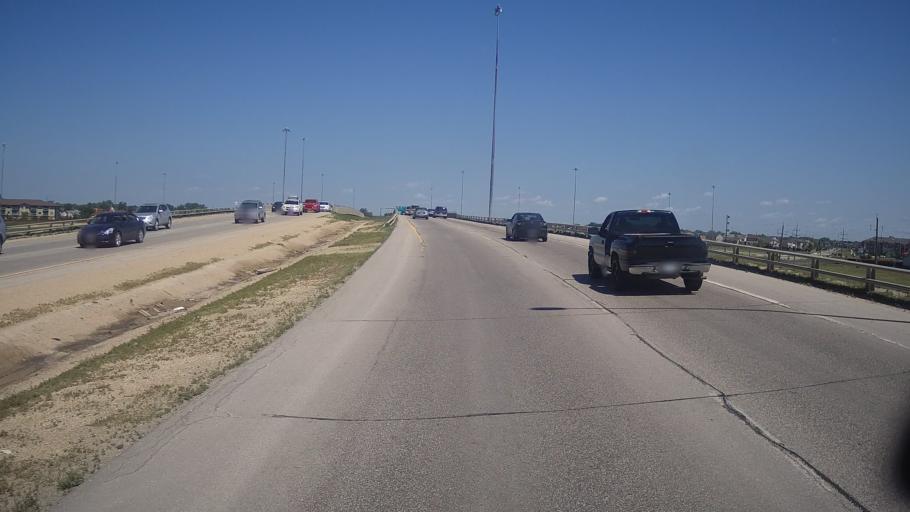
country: CA
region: Manitoba
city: Winnipeg
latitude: 49.9093
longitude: -97.0575
